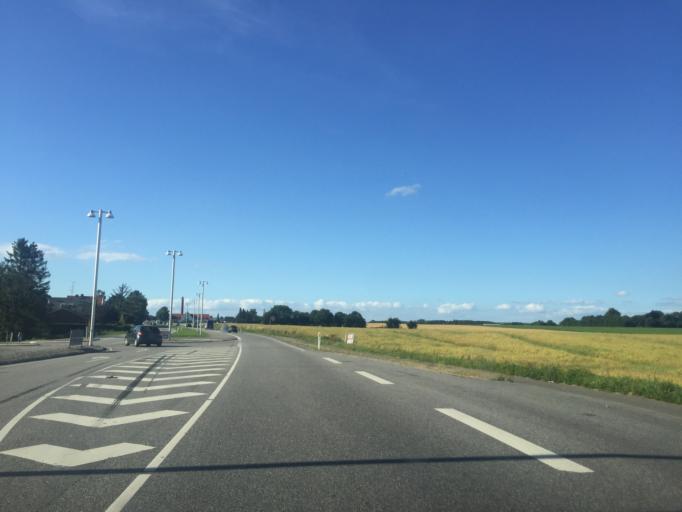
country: DK
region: Zealand
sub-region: Guldborgsund Kommune
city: Norre Alslev
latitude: 54.8495
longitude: 11.8580
